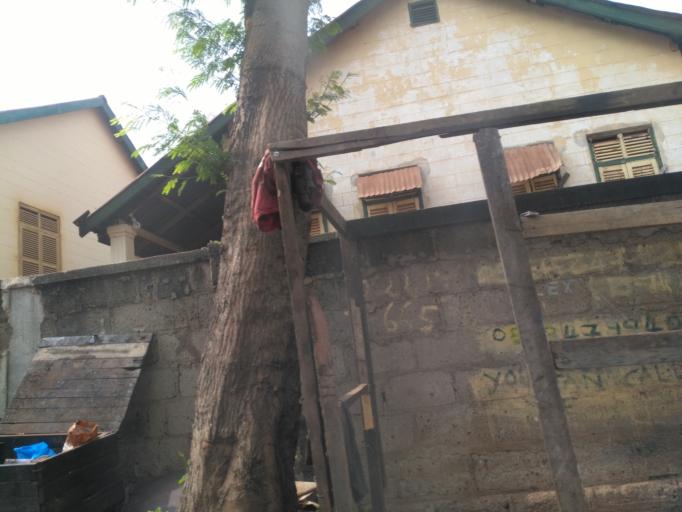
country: GH
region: Ashanti
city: Kumasi
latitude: 6.7072
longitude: -1.6226
